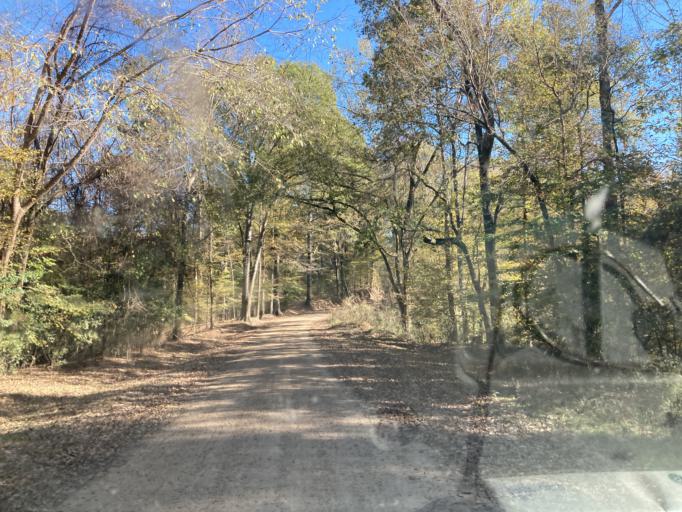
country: US
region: Mississippi
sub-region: Yazoo County
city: Yazoo City
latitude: 32.7769
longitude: -90.4075
